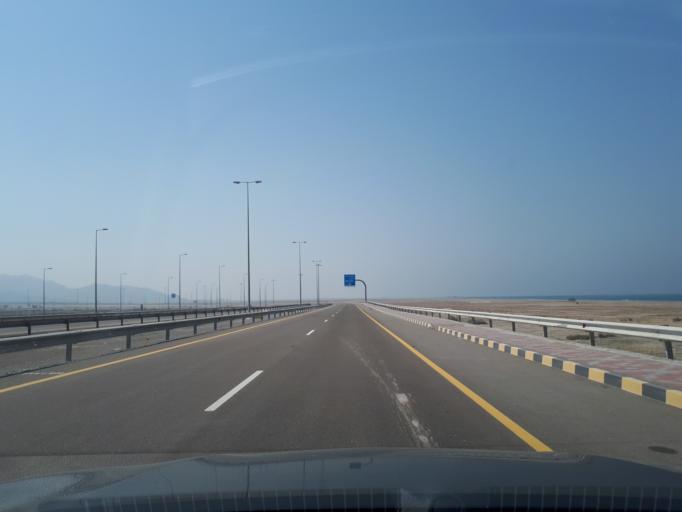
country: AE
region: Al Fujayrah
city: Al Fujayrah
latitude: 24.9471
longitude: 56.3807
